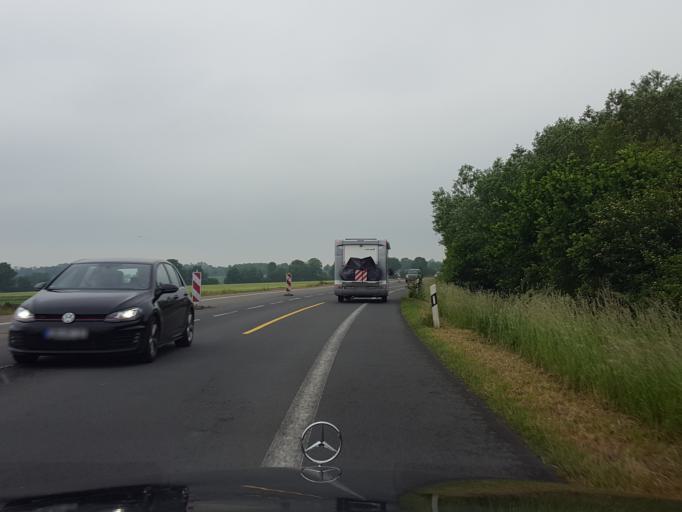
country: DE
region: North Rhine-Westphalia
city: Olfen
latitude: 51.7012
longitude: 7.3889
